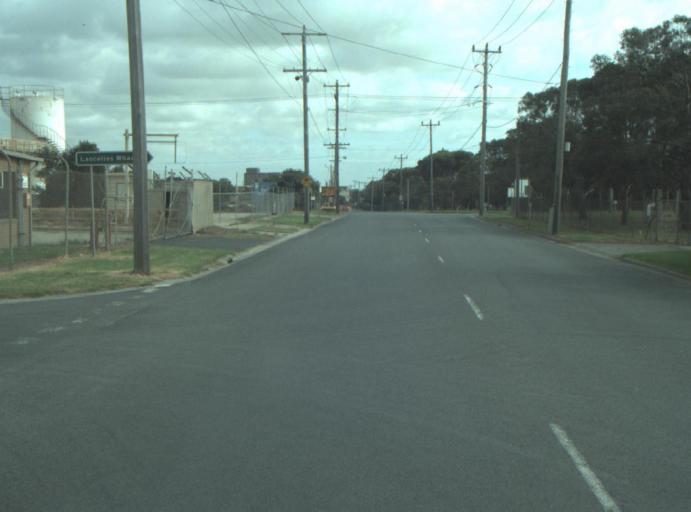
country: AU
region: Victoria
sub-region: Greater Geelong
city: Bell Park
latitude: -38.0919
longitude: 144.3732
